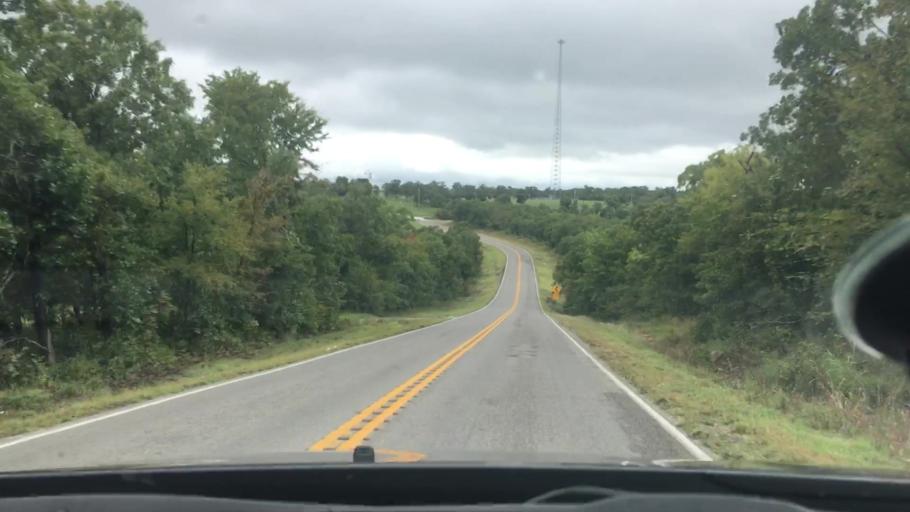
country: US
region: Oklahoma
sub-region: Sequoyah County
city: Vian
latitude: 35.6246
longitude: -94.9620
